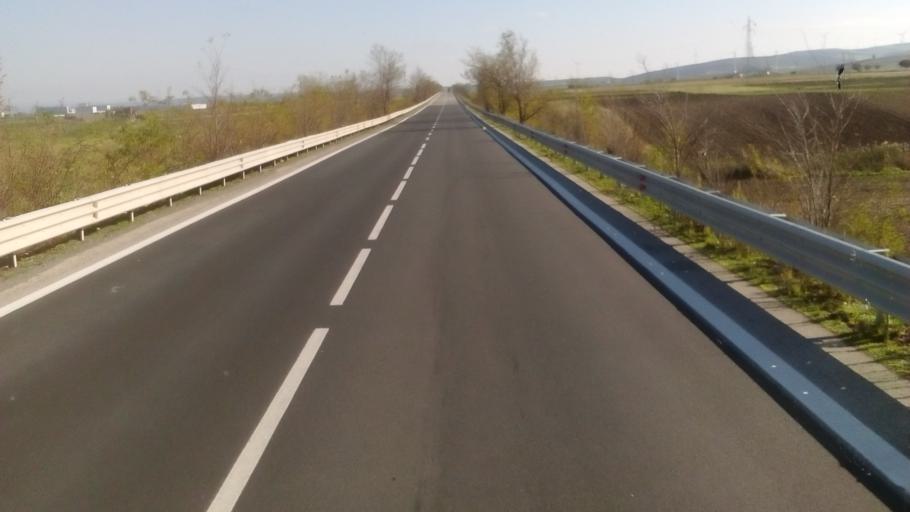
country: IT
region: Basilicate
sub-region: Provincia di Potenza
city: Zona 179
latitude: 41.0808
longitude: 15.6278
